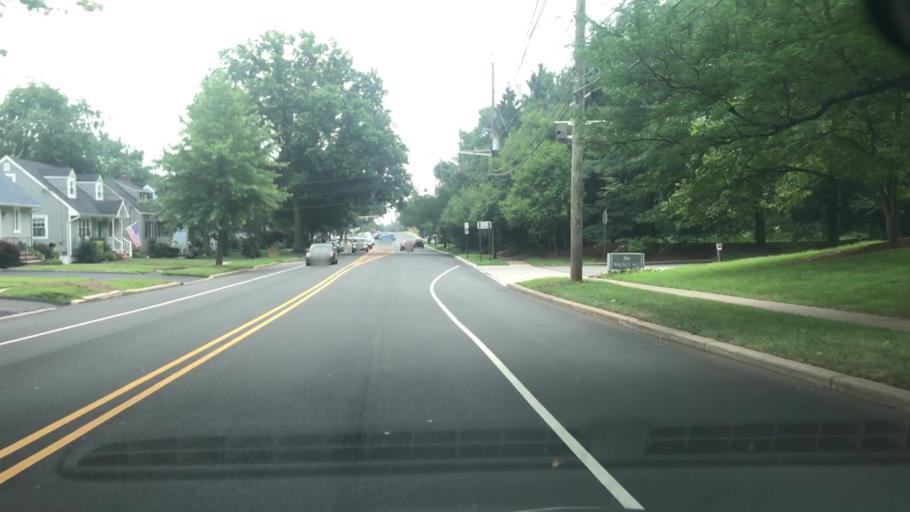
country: US
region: New Jersey
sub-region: Union County
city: Clark
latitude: 40.6363
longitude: -74.3043
